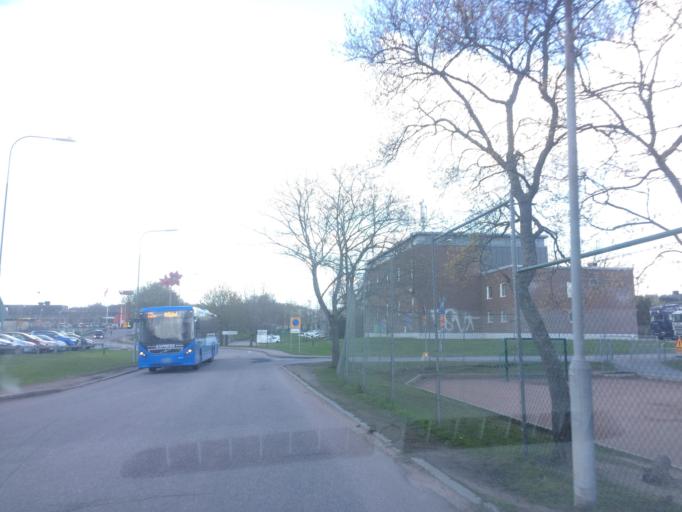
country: SE
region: Vaestra Goetaland
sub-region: Goteborg
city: Gardsten
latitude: 57.7924
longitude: 11.9913
